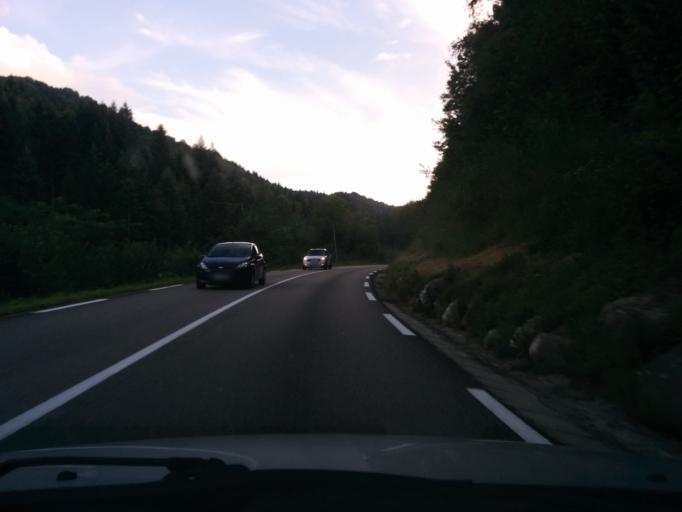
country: FR
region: Rhone-Alpes
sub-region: Departement de l'Isere
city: Saint-Aupre
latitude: 45.3480
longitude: 5.6683
